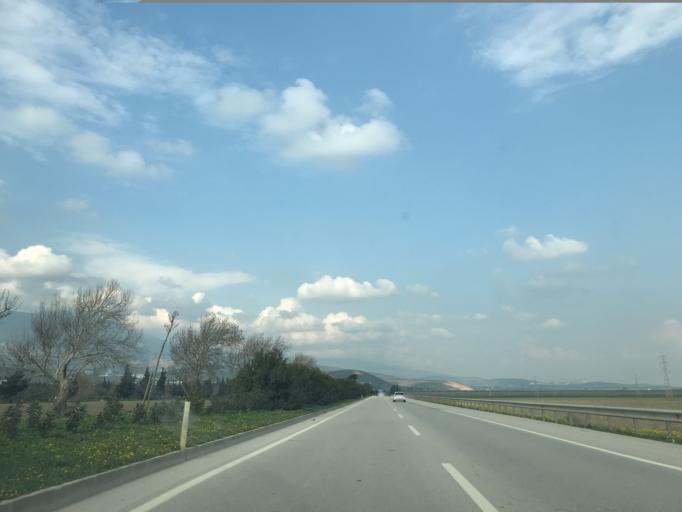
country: TR
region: Hatay
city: Serinyol
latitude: 36.4180
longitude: 36.2730
